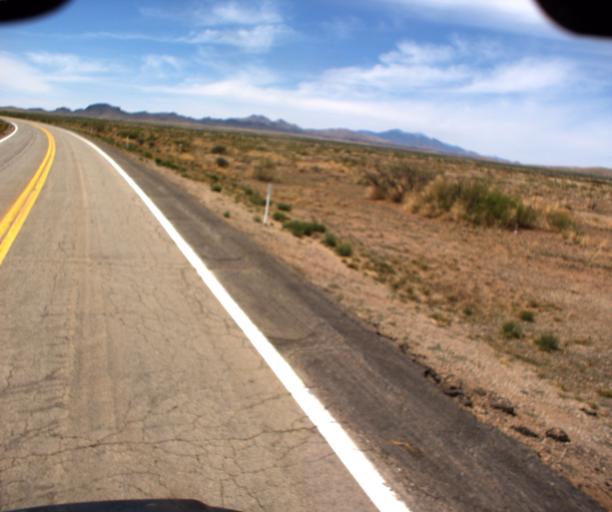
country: US
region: Arizona
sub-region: Cochise County
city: Willcox
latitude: 32.3716
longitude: -109.6281
